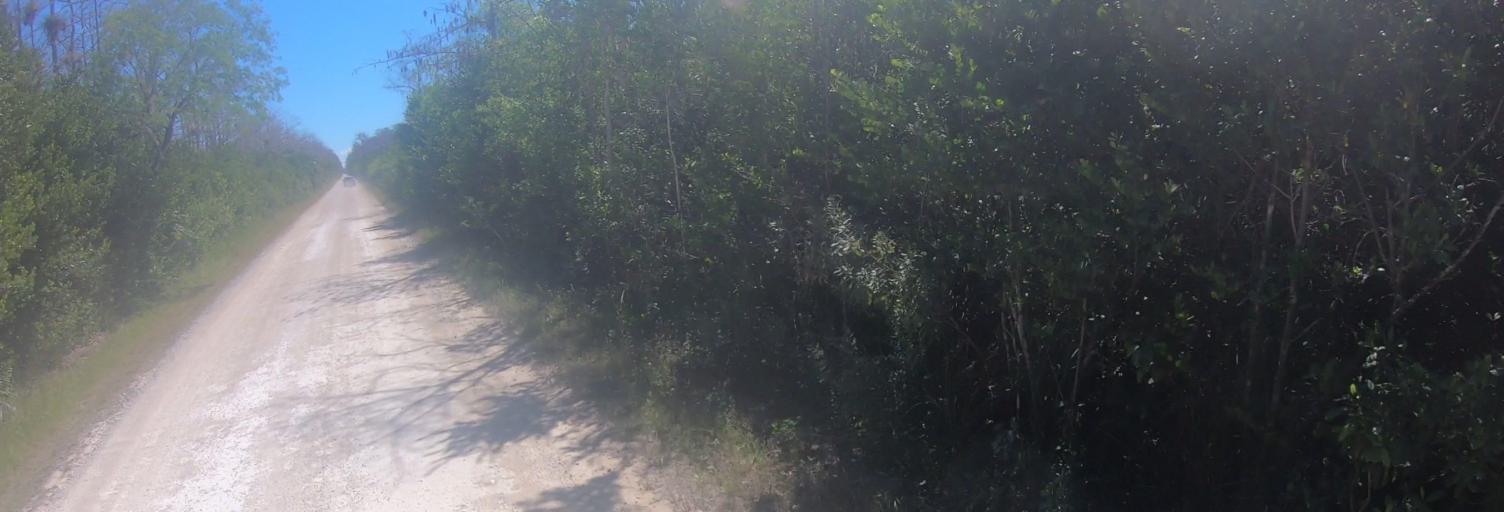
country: US
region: Florida
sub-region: Miami-Dade County
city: The Hammocks
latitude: 25.7534
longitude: -80.9751
